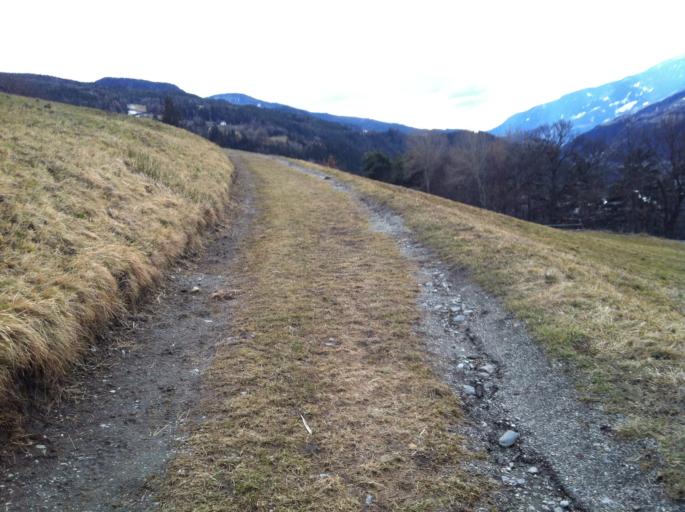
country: IT
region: Trentino-Alto Adige
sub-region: Bolzano
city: Bressanone
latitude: 46.6970
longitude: 11.6624
